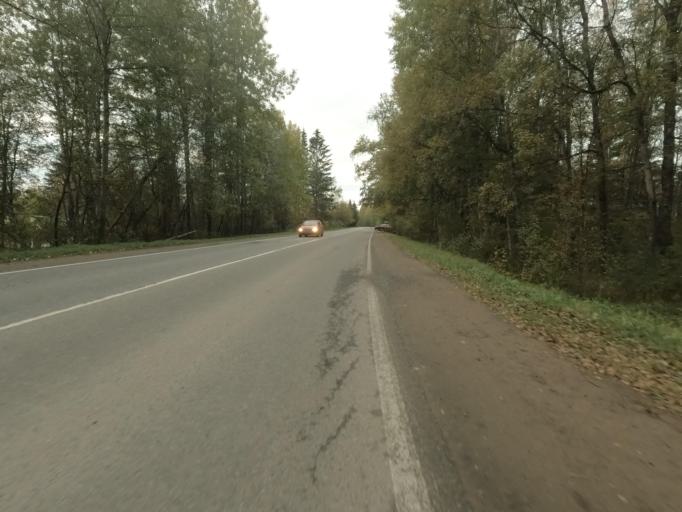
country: RU
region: Leningrad
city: Pavlovo
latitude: 59.7886
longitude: 30.9626
